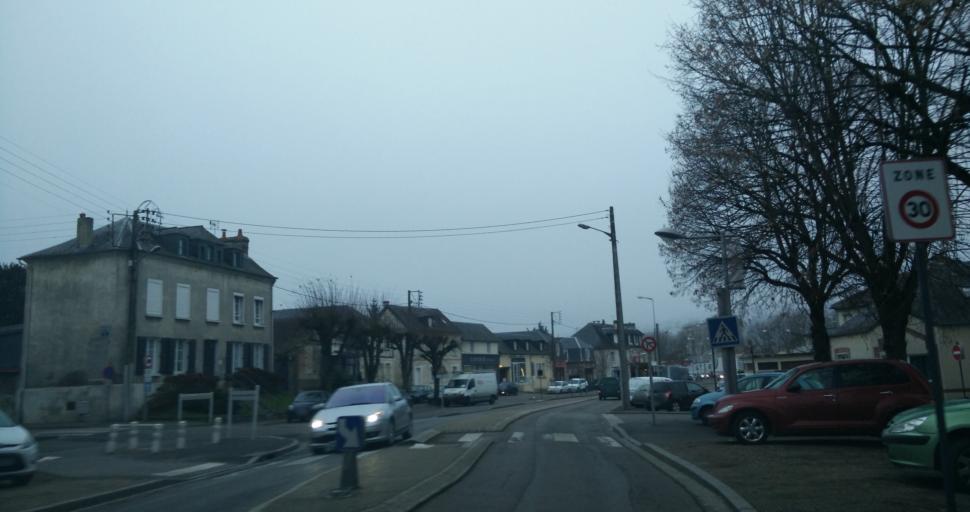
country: FR
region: Haute-Normandie
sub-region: Departement de l'Eure
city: Louviers
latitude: 49.2100
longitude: 1.1673
